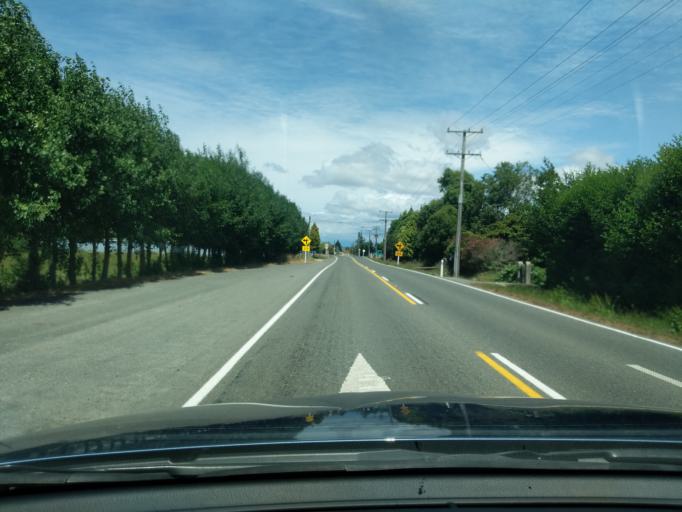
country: NZ
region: Tasman
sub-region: Tasman District
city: Motueka
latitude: -41.0891
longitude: 172.9968
